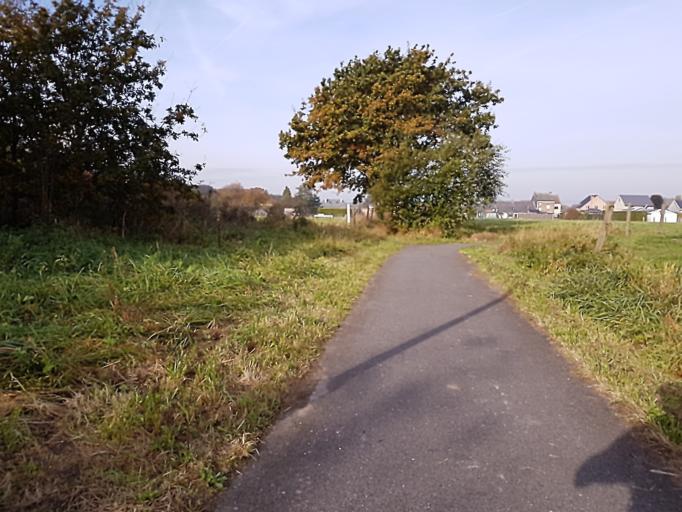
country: BE
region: Flanders
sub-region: Provincie Antwerpen
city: Sint-Katelijne-Waver
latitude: 51.0678
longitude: 4.5705
